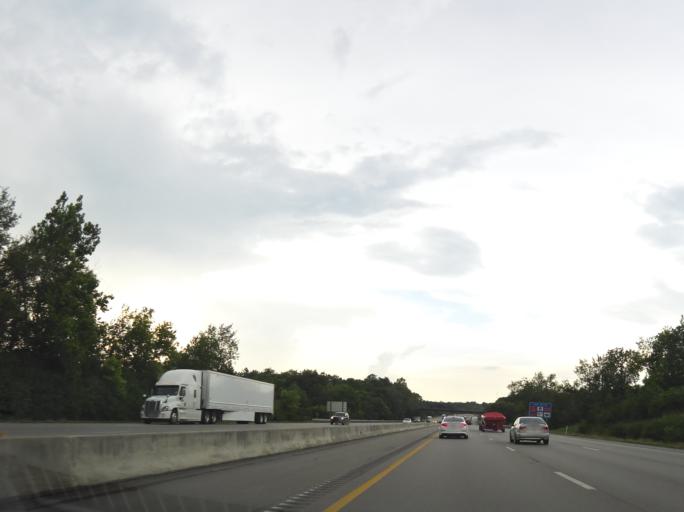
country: US
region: Kentucky
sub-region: Fayette County
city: Lexington
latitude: 37.9474
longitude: -84.3844
